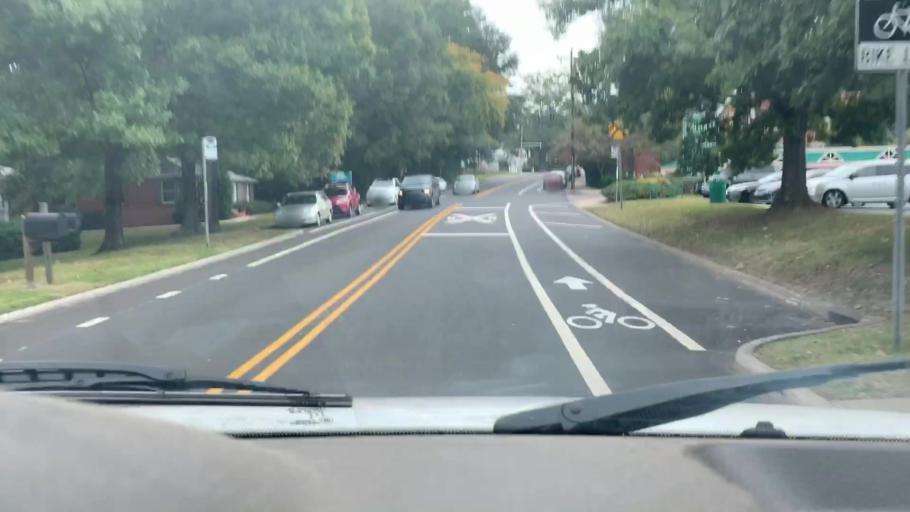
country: US
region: North Carolina
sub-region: Gaston County
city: Davidson
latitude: 35.5026
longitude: -80.8501
